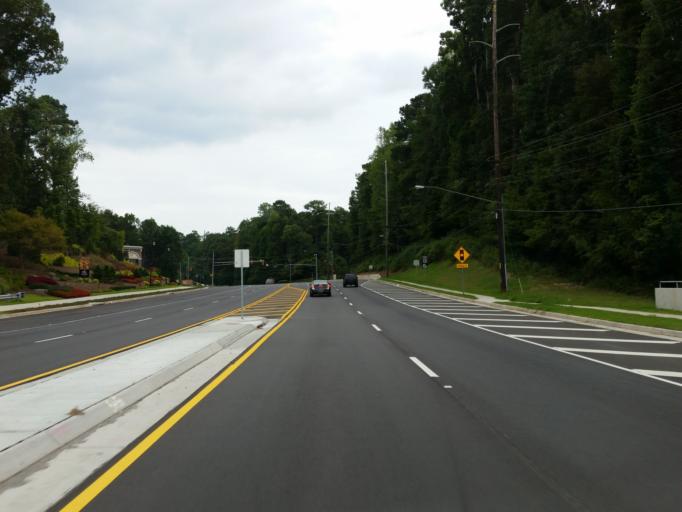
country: US
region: Georgia
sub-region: Cobb County
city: Vinings
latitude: 33.8665
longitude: -84.4529
